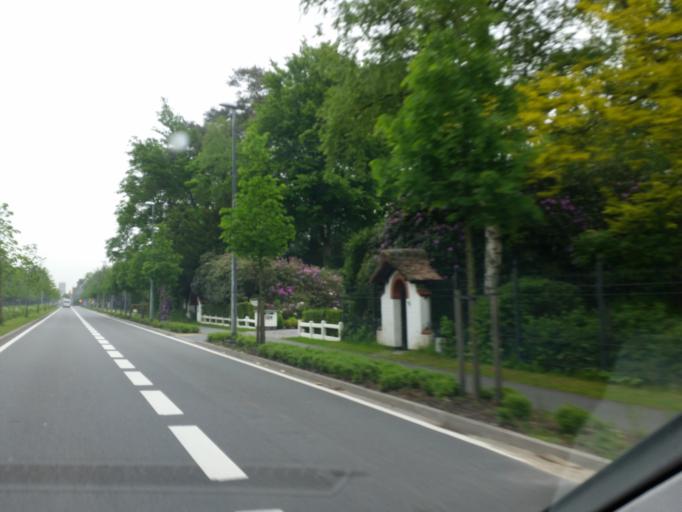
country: BE
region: Flanders
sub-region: Provincie Antwerpen
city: Brasschaat
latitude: 51.2821
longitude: 4.4802
